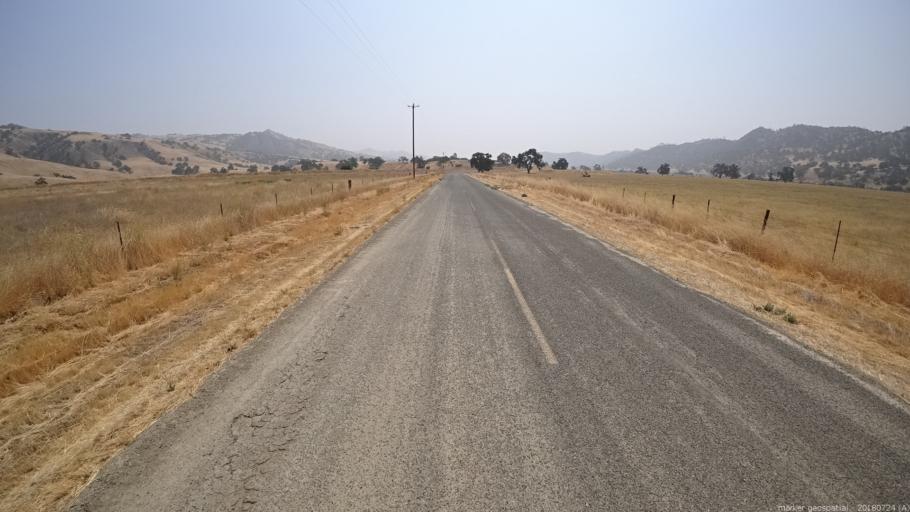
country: US
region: California
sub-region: Monterey County
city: King City
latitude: 36.1825
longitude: -120.8000
